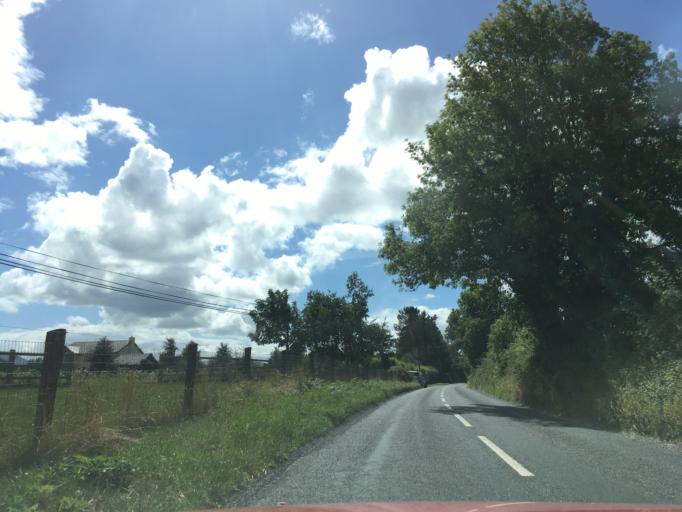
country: IE
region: Munster
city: Cahir
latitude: 52.3455
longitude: -7.9449
